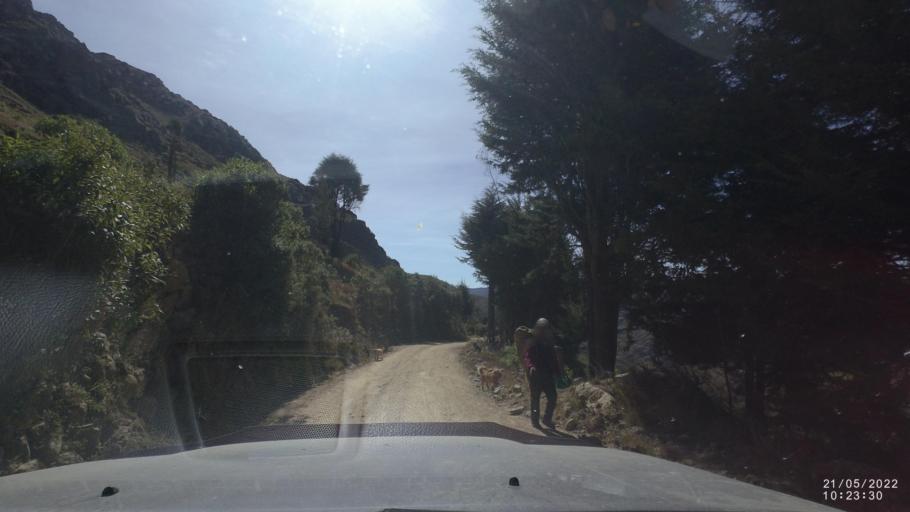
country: BO
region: Cochabamba
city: Colomi
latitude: -17.3253
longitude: -65.9513
